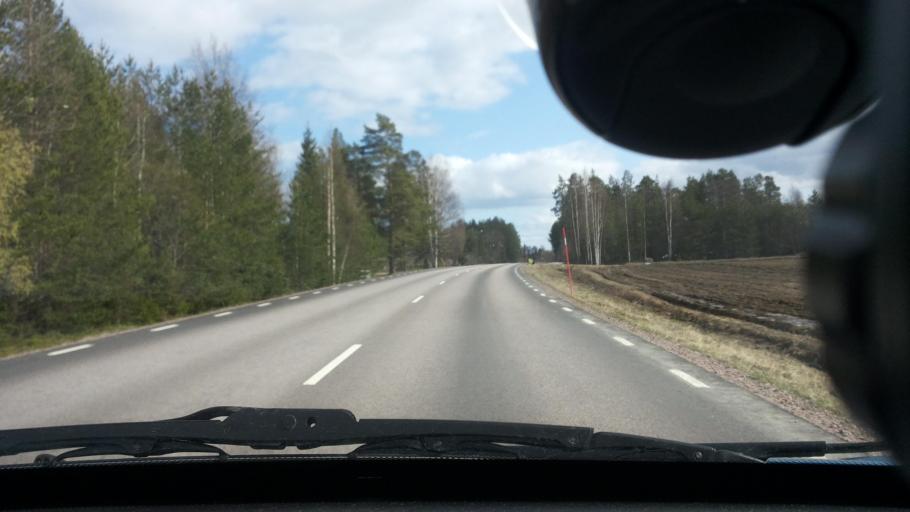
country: SE
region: Norrbotten
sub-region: Lulea Kommun
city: Sodra Sunderbyn
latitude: 65.6488
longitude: 21.8760
